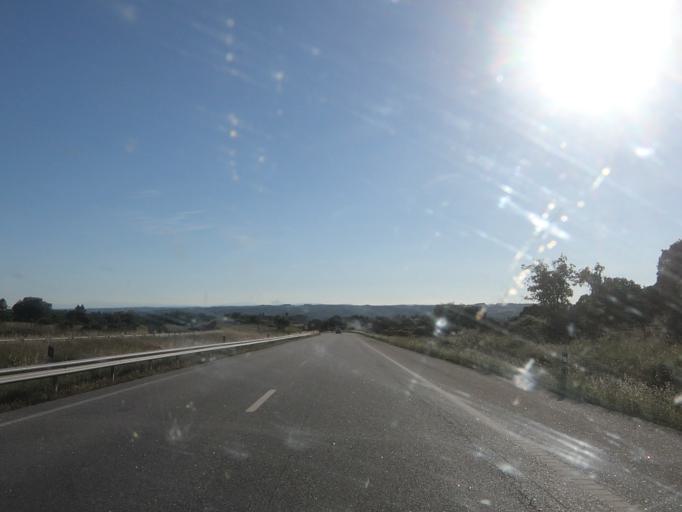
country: ES
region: Castille and Leon
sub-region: Provincia de Salamanca
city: Fuentes de Onoro
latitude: 40.6153
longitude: -6.8804
